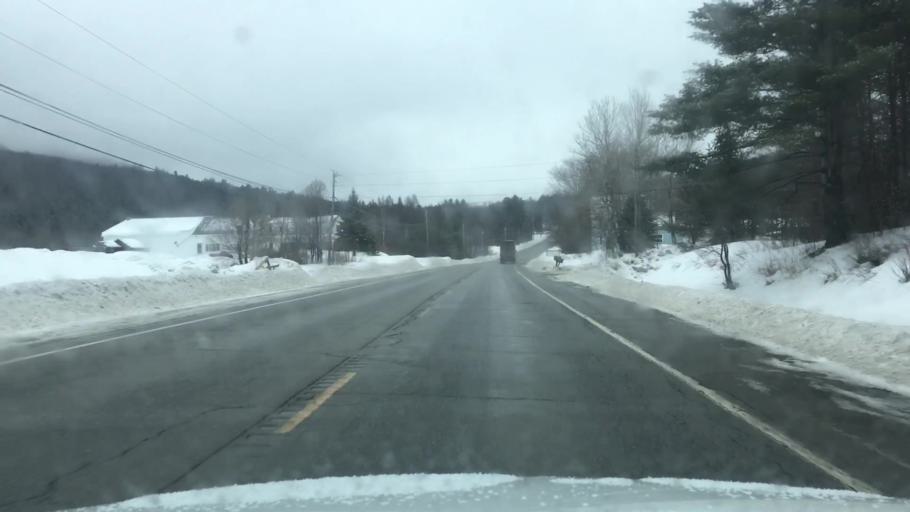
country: US
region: Maine
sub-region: Oxford County
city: Peru
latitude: 44.5685
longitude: -70.3735
